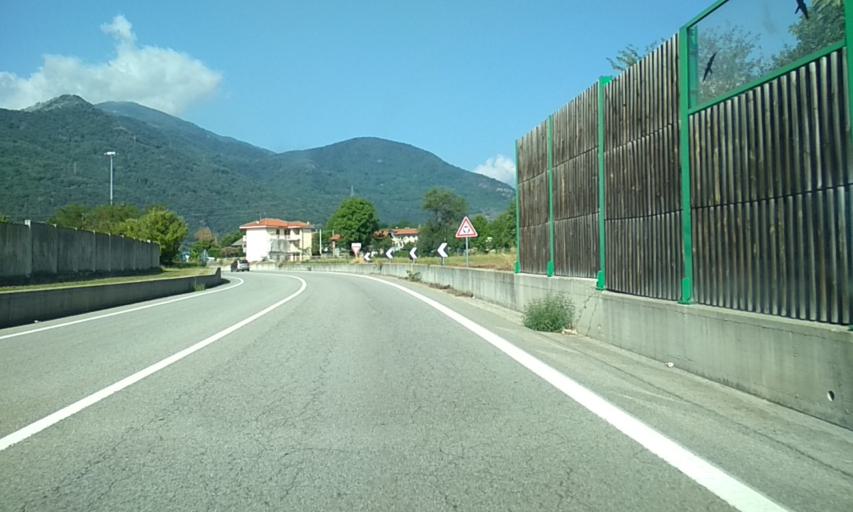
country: IT
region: Piedmont
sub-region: Provincia di Torino
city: Cuorgne
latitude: 45.4028
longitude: 7.6470
